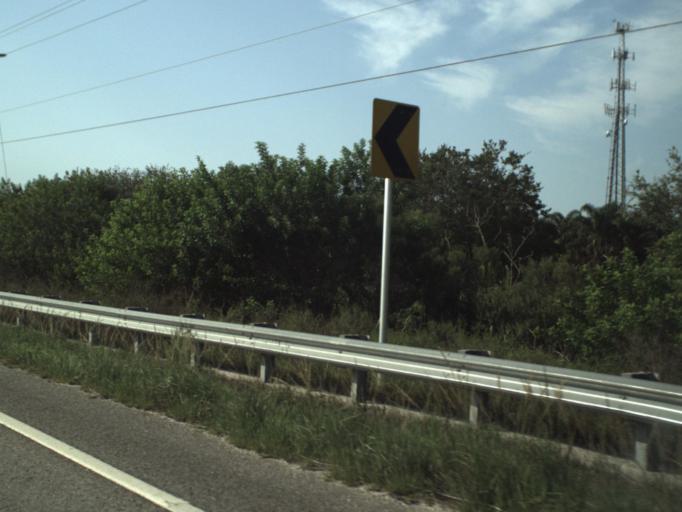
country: US
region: Florida
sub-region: Palm Beach County
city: South Bay
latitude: 26.6995
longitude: -80.8240
